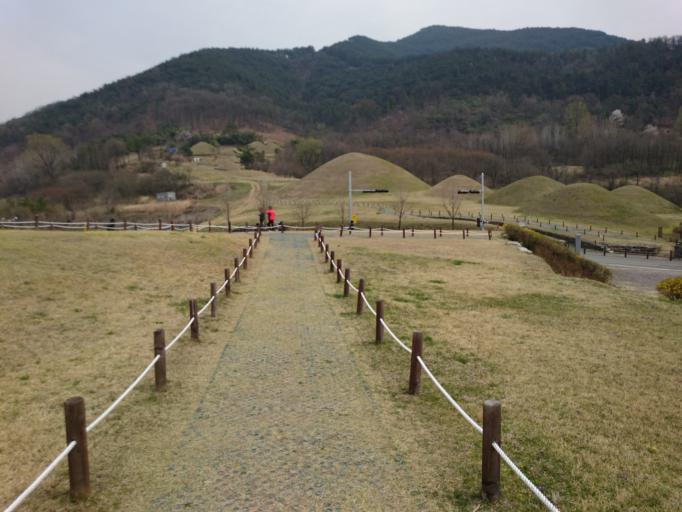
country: KR
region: Gyeongsangnam-do
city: Changnyeong
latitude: 35.5464
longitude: 128.5043
